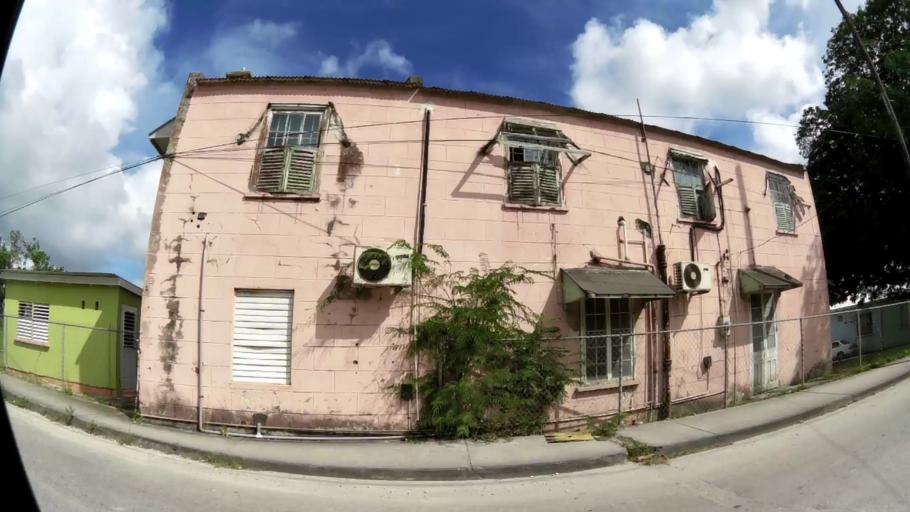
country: BB
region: Saint Michael
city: Bridgetown
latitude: 13.0992
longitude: -59.5926
